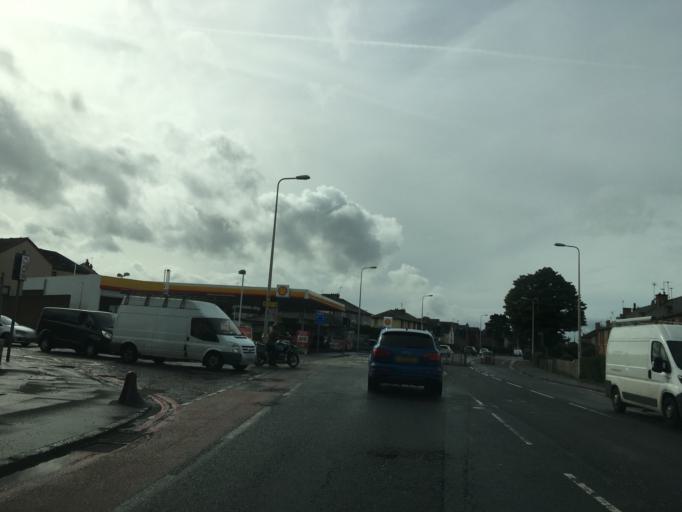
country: GB
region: Scotland
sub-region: Edinburgh
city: Colinton
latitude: 55.9302
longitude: -3.2557
